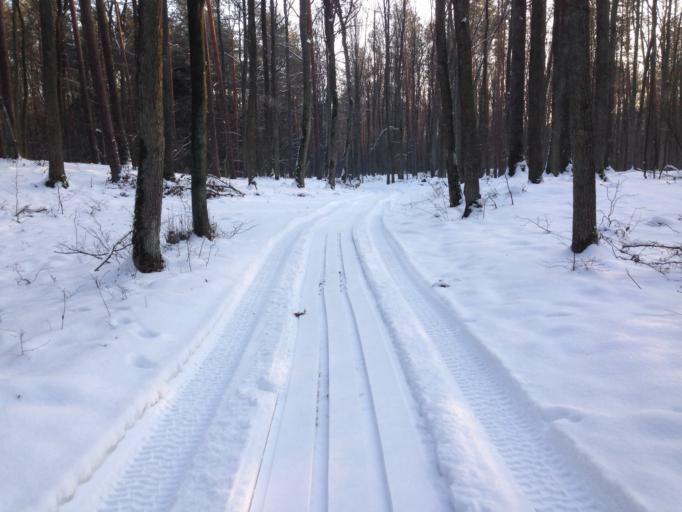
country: PL
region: Kujawsko-Pomorskie
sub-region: Powiat brodnicki
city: Gorzno
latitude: 53.1966
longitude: 19.6698
